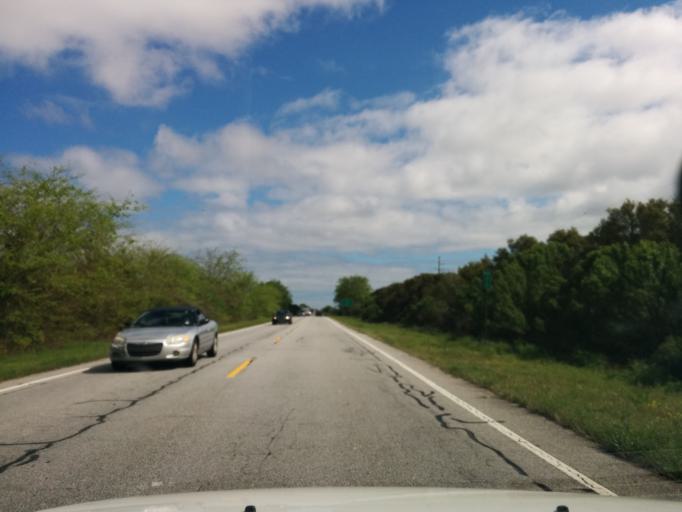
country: US
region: Georgia
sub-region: Glynn County
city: Brunswick
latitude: 31.0693
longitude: -81.4605
